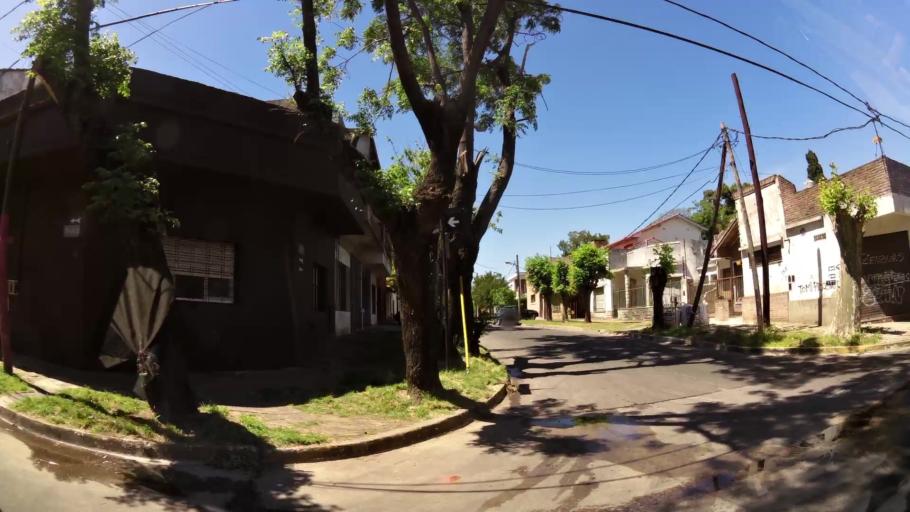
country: AR
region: Buenos Aires
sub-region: Partido de Quilmes
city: Quilmes
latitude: -34.7156
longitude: -58.2882
